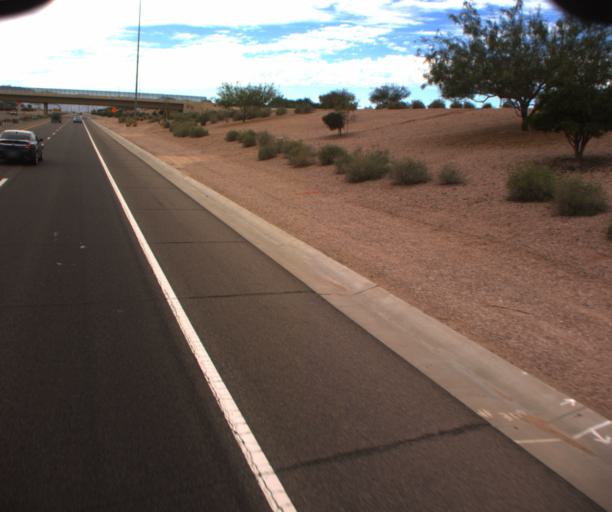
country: US
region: Arizona
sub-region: Maricopa County
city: Guadalupe
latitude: 33.2958
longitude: -111.9778
